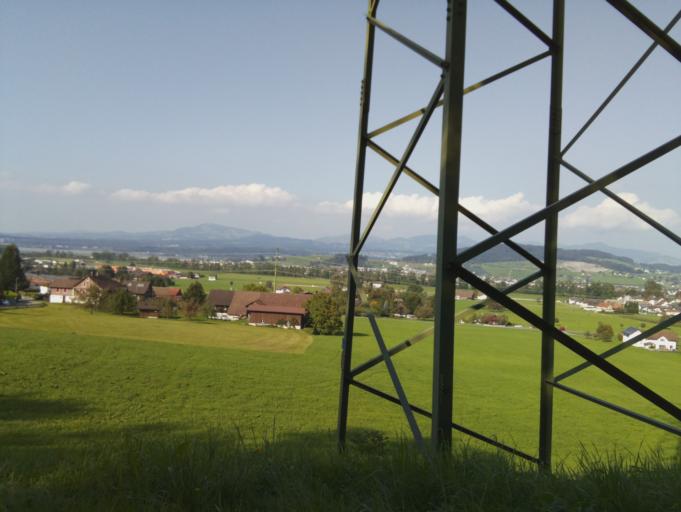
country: CH
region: Schwyz
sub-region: Bezirk March
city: Lachen
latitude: 47.1715
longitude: 8.8809
